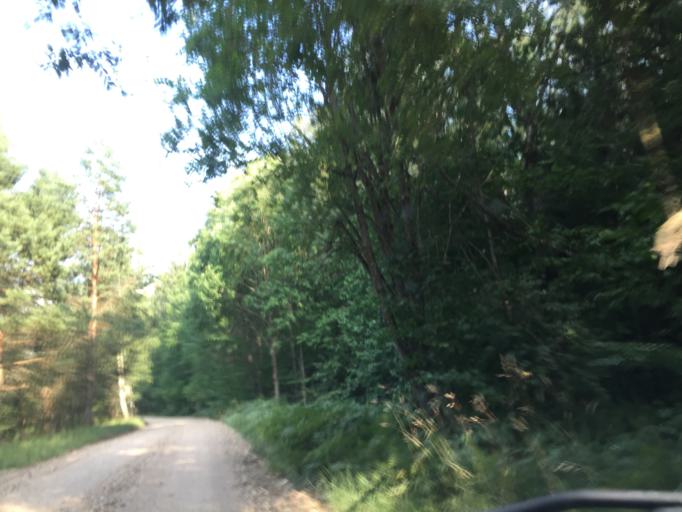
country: LT
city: Zagare
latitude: 56.4482
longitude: 23.1288
